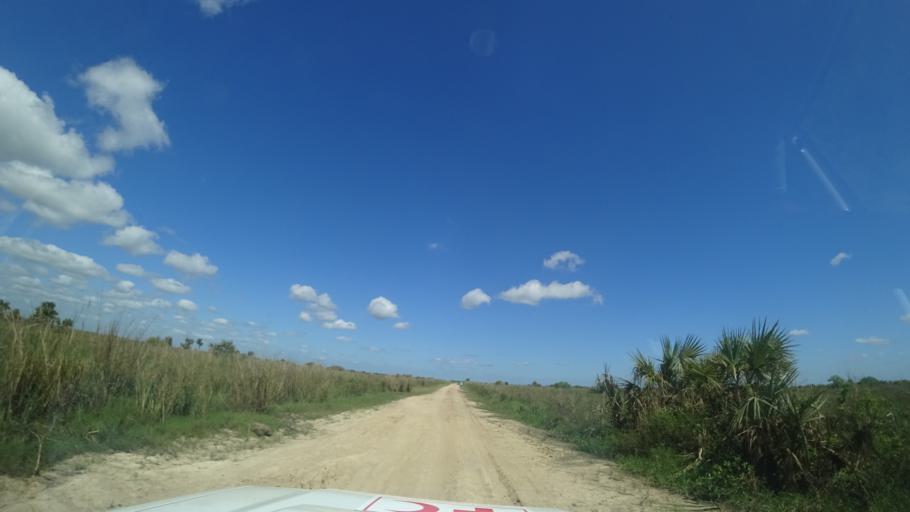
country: MZ
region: Sofala
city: Dondo
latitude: -19.3893
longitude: 34.5784
